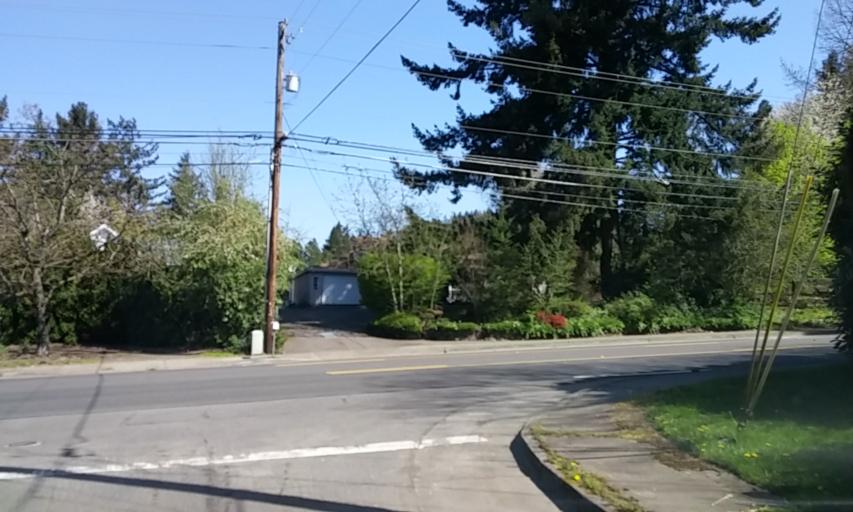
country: US
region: Oregon
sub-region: Washington County
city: West Haven-Sylvan
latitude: 45.5085
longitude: -122.7662
